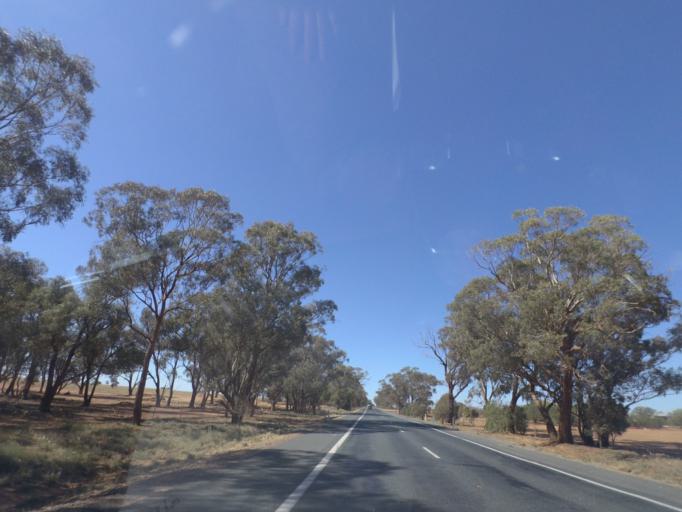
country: AU
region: New South Wales
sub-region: Bland
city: West Wyalong
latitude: -34.2059
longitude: 147.1096
